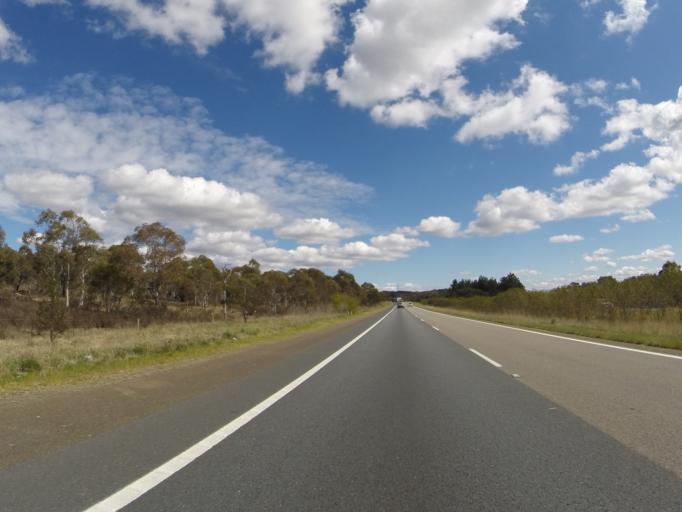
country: AU
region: New South Wales
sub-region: Goulburn Mulwaree
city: Goulburn
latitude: -34.7352
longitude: 149.9569
